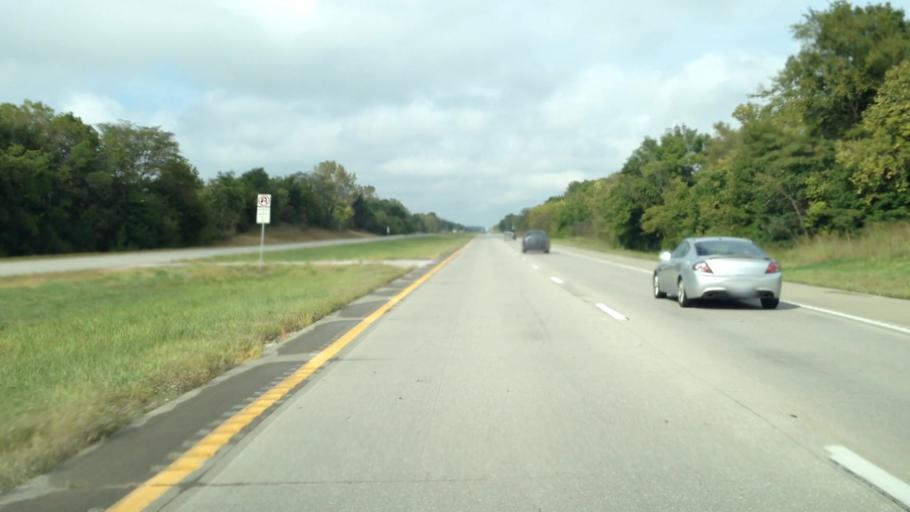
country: US
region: Missouri
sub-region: Clay County
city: Kearney
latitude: 39.3924
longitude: -94.3591
